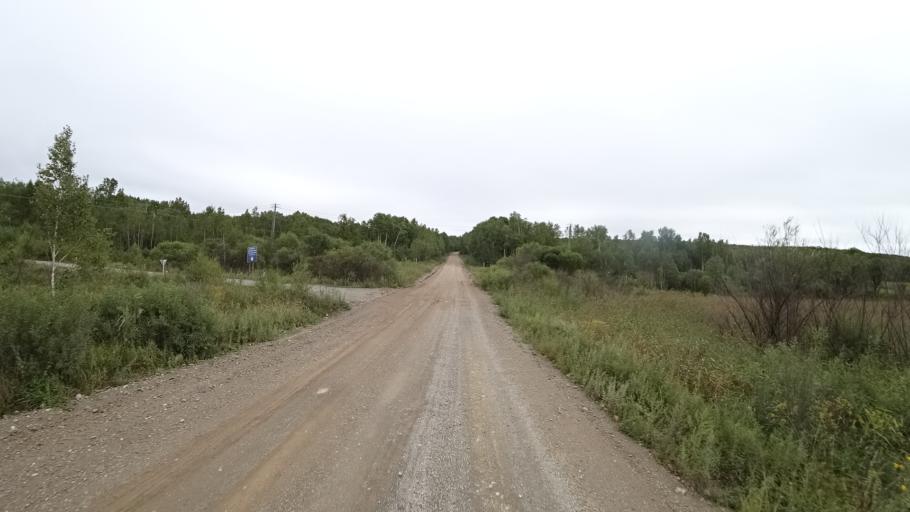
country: RU
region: Primorskiy
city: Ivanovka
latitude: 44.0291
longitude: 132.5120
